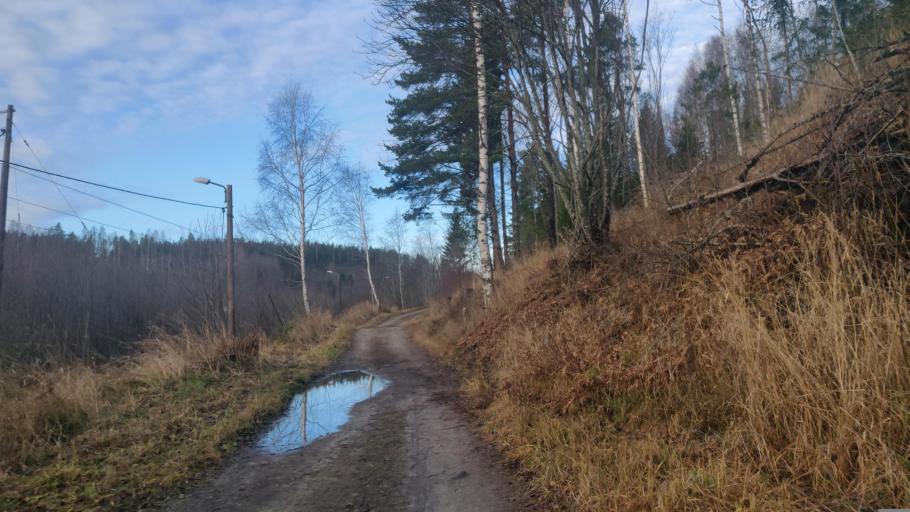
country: SE
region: Vaesternorrland
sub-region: Sundsvalls Kommun
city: Nolby
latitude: 62.2983
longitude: 17.3590
